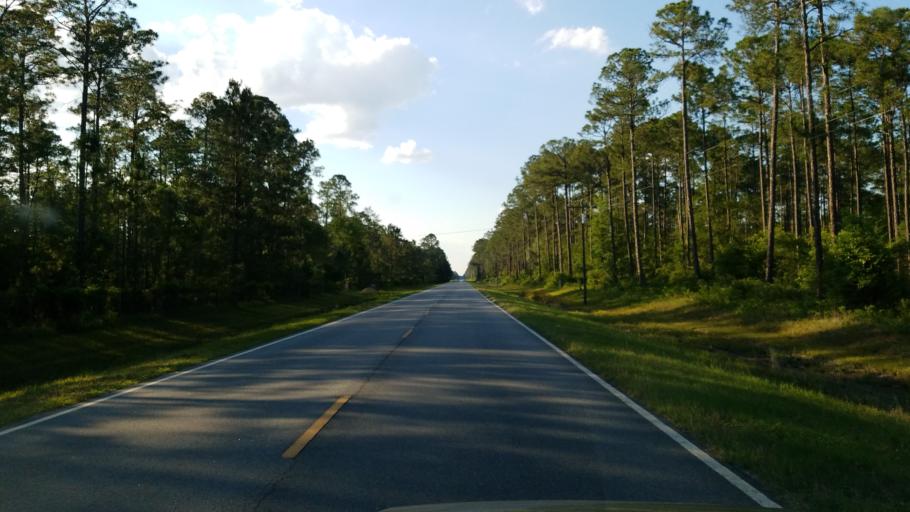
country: US
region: Georgia
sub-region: Lanier County
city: Lakeland
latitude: 31.0887
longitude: -83.0769
